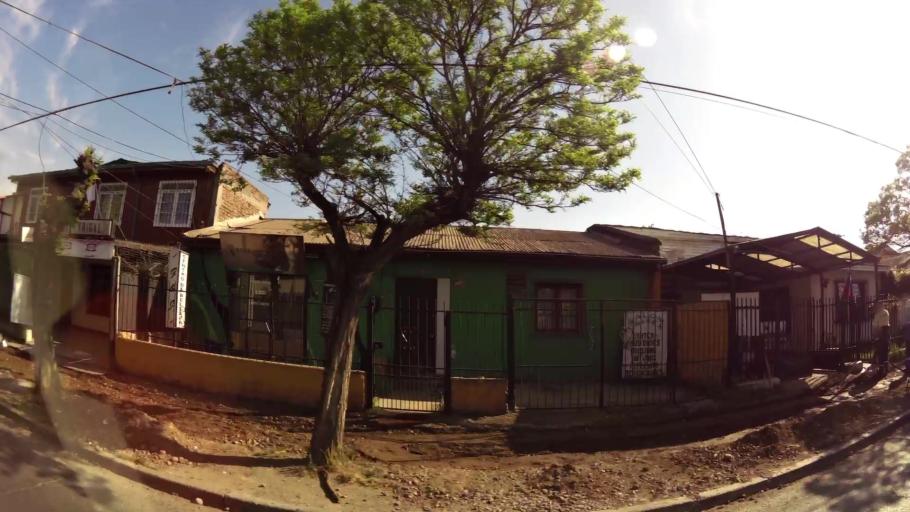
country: CL
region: Santiago Metropolitan
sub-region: Provincia de Santiago
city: La Pintana
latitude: -33.5617
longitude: -70.5952
